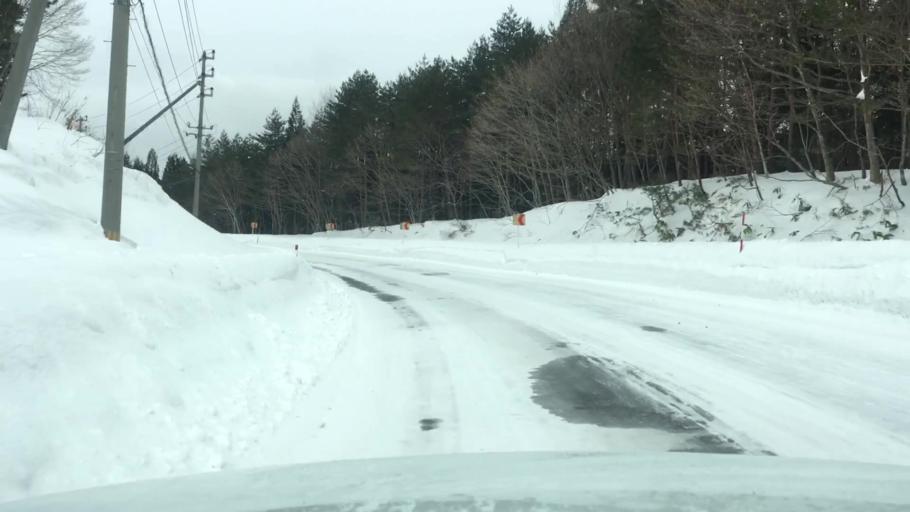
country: JP
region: Akita
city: Hanawa
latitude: 39.9946
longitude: 140.9951
